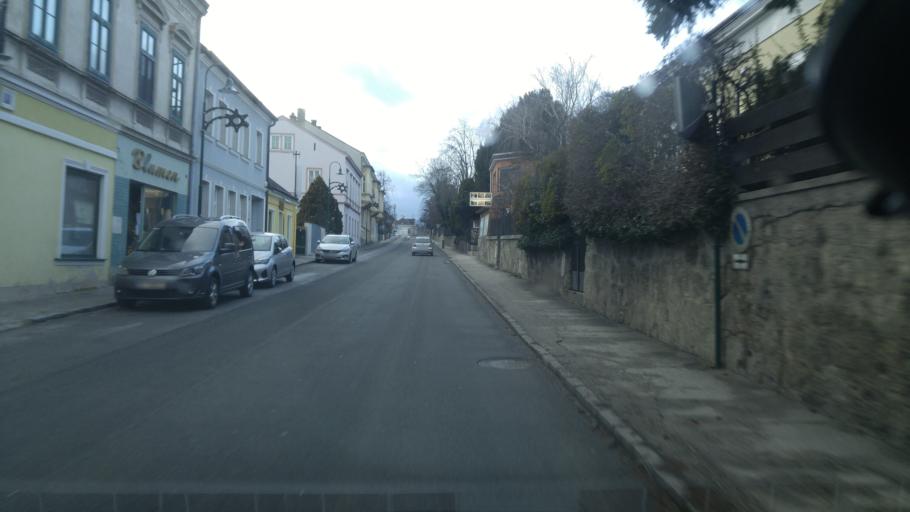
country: AT
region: Lower Austria
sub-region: Politischer Bezirk Baden
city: Bad Voslau
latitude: 47.9649
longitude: 16.2120
